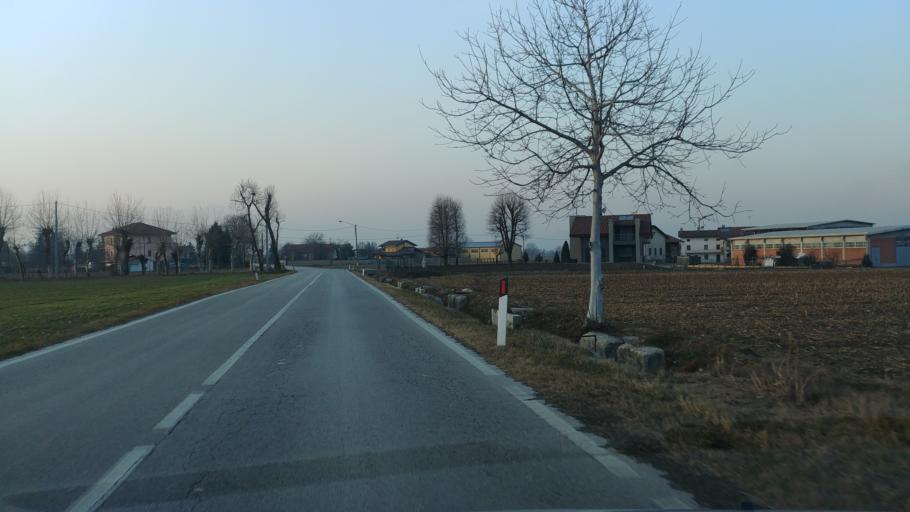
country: IT
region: Piedmont
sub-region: Provincia di Cuneo
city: Roata Rossi
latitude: 44.4227
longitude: 7.5283
